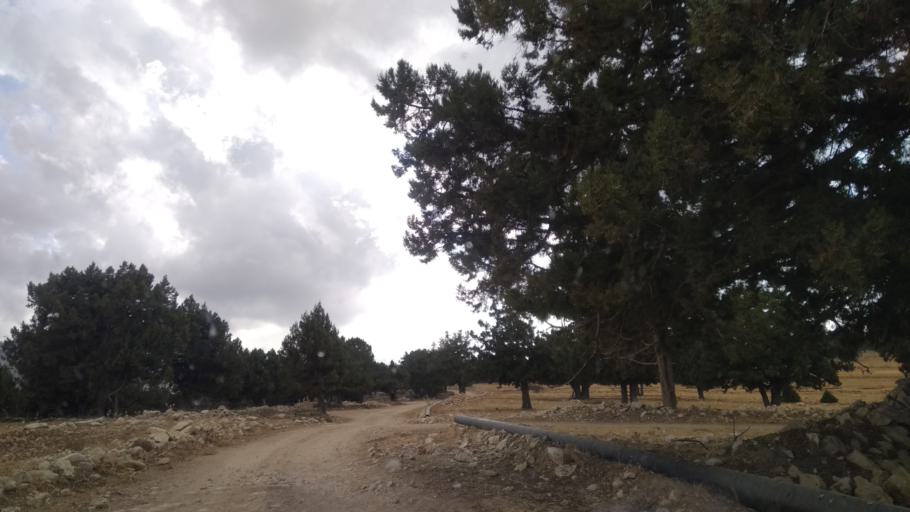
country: TR
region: Mersin
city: Sarikavak
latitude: 36.5692
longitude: 33.7441
